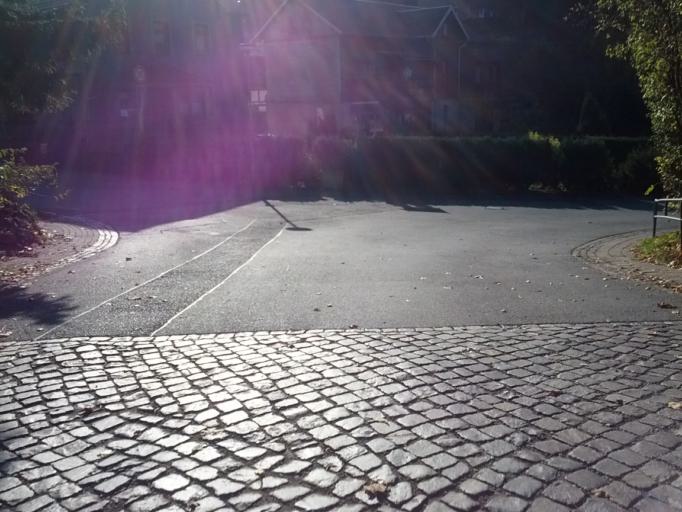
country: DE
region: Thuringia
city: Thal
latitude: 50.9127
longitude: 10.4002
